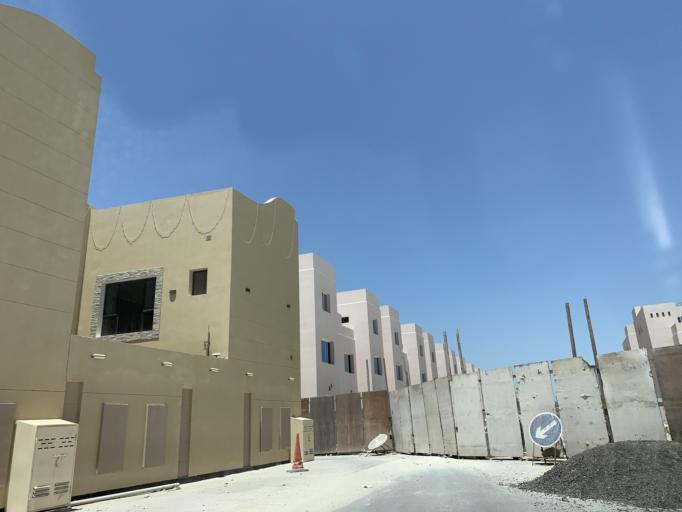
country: BH
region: Manama
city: Jidd Hafs
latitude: 26.2325
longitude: 50.4926
